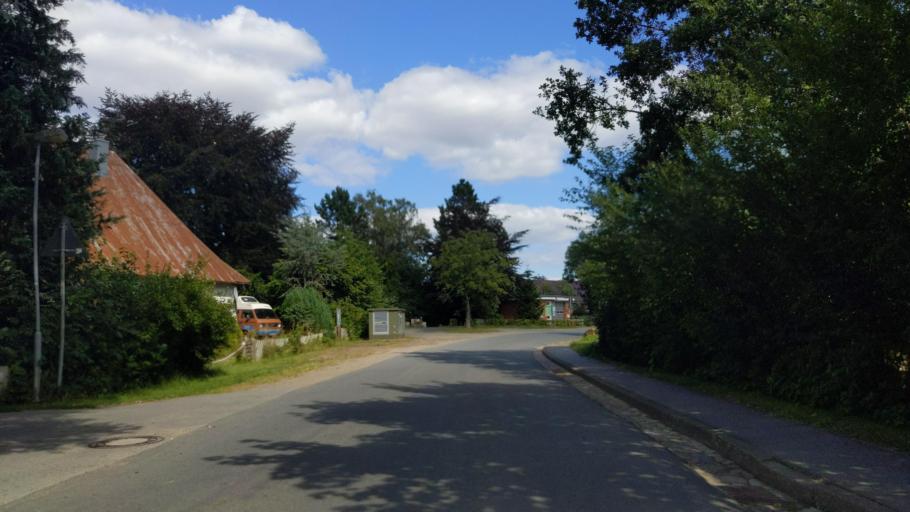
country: DE
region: Schleswig-Holstein
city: Stockelsdorf
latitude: 53.9151
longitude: 10.6036
